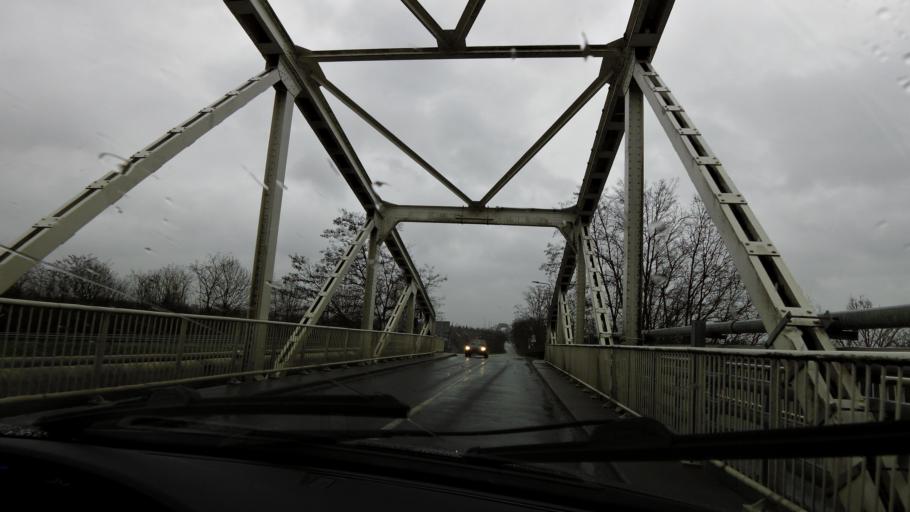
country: NL
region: Limburg
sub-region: Gemeente Stein
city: Stein
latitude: 50.9707
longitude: 5.7520
